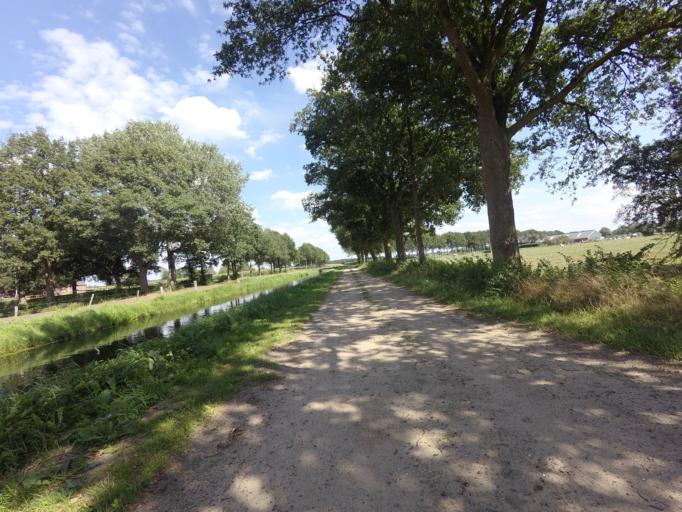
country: NL
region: Overijssel
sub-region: Gemeente Deventer
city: Schalkhaar
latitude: 52.2794
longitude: 6.2410
